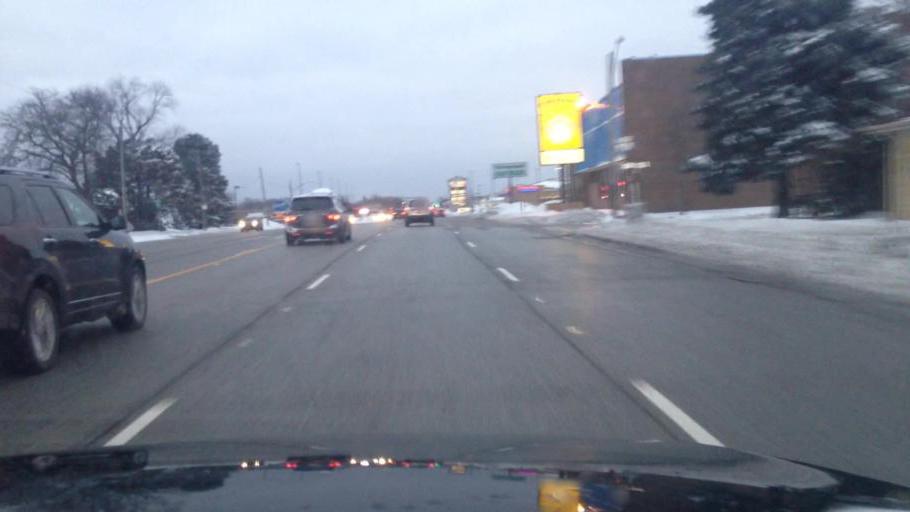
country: US
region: Illinois
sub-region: Cook County
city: Niles
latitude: 42.0407
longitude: -87.8117
